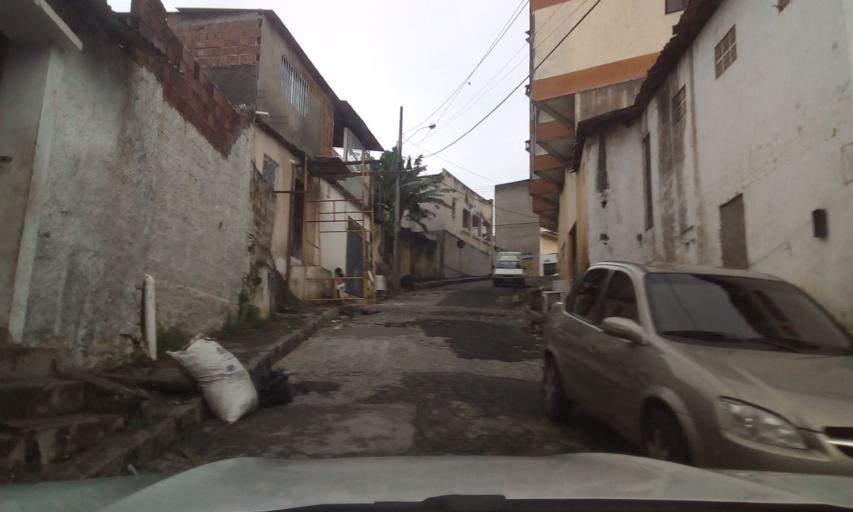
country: BR
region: Paraiba
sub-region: Joao Pessoa
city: Joao Pessoa
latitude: -7.1223
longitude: -34.8860
